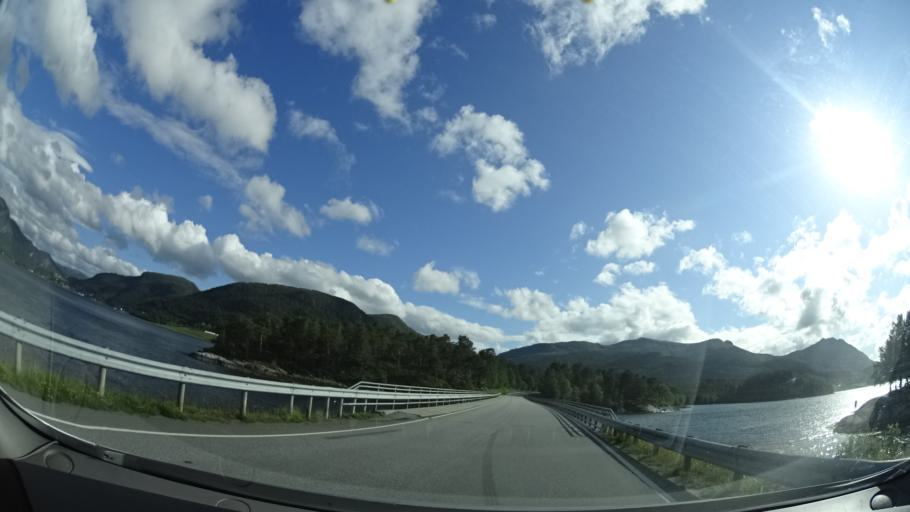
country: NO
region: More og Romsdal
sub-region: Aure
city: Aure
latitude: 63.1412
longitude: 8.5327
